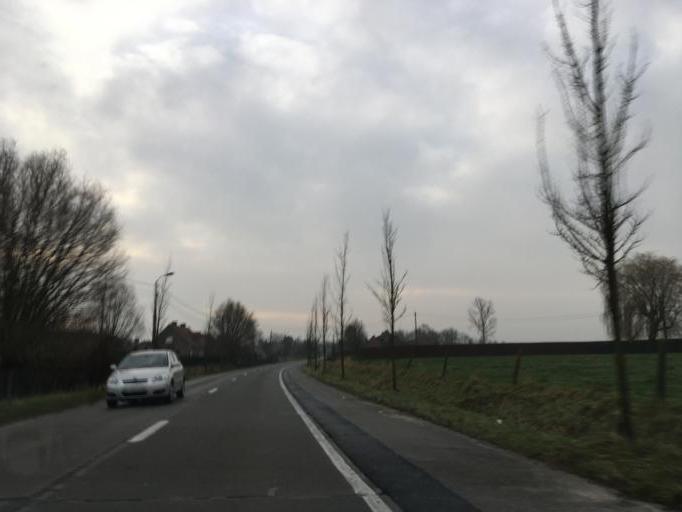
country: BE
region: Flanders
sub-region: Provincie West-Vlaanderen
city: Anzegem
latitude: 50.8490
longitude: 3.4649
